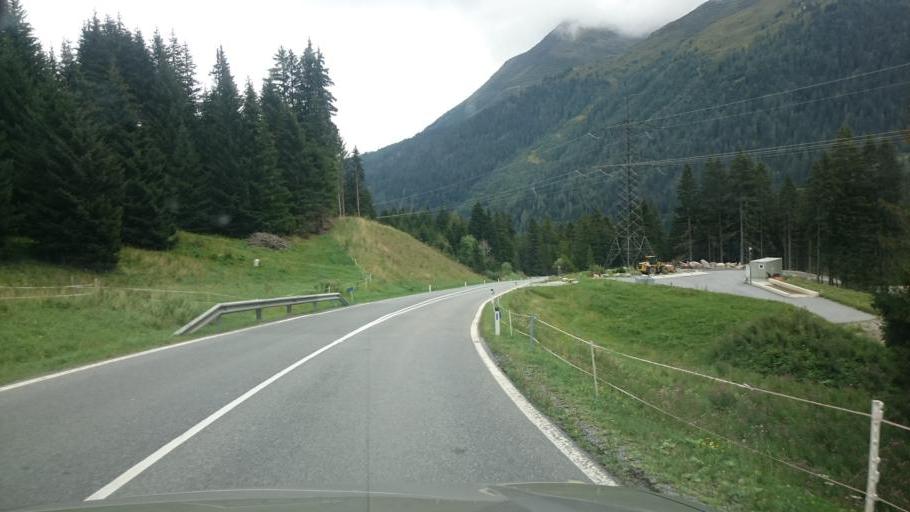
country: AT
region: Tyrol
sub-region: Politischer Bezirk Landeck
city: Sankt Anton am Arlberg
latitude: 47.1235
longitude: 10.2422
